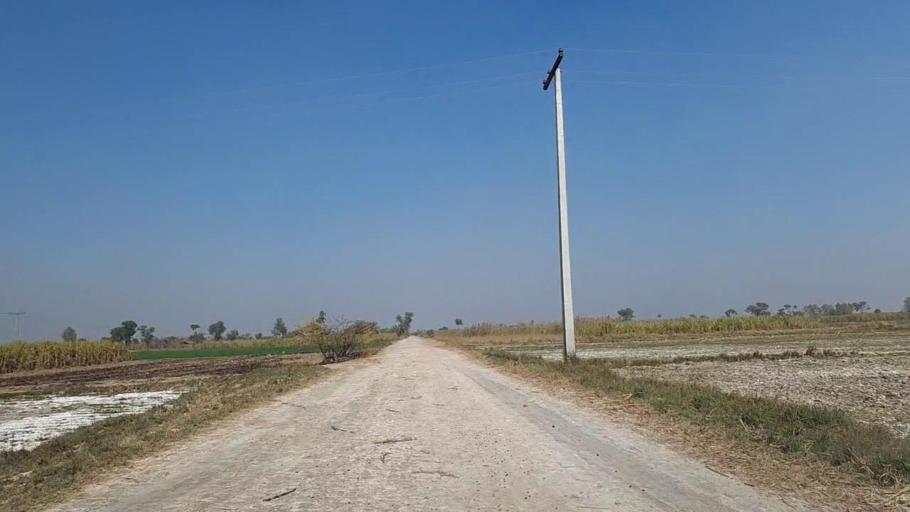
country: PK
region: Sindh
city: Daur
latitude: 26.4897
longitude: 68.3385
